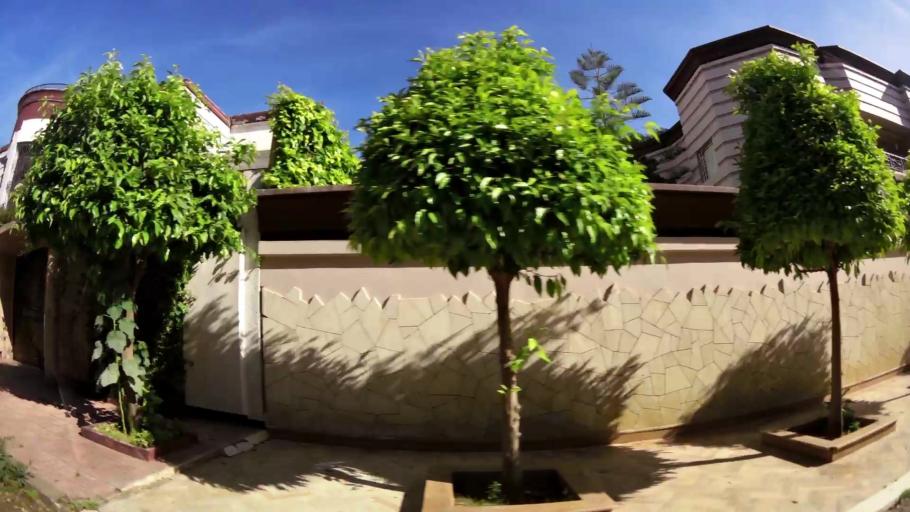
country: MA
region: Oriental
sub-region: Oujda-Angad
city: Oujda
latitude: 34.6650
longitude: -1.9030
